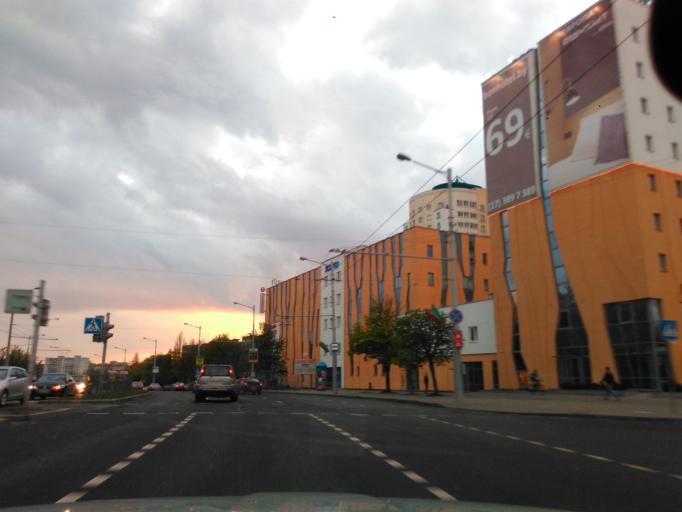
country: BY
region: Minsk
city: Minsk
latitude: 53.9101
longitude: 27.5067
